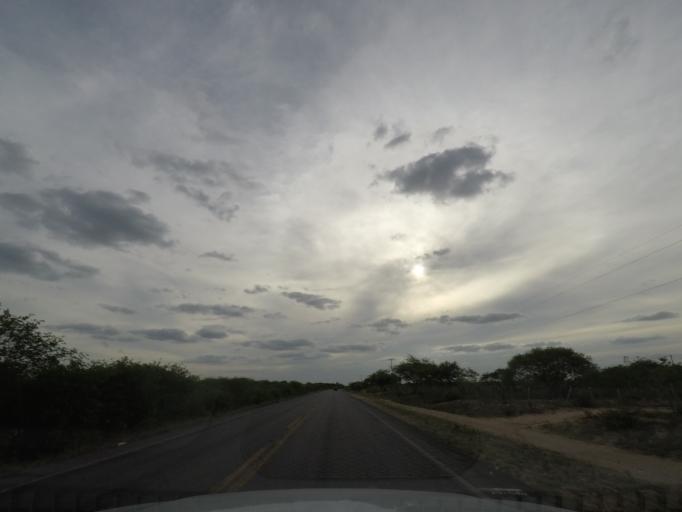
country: BR
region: Bahia
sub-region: Ipira
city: Ipira
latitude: -12.3302
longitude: -39.9372
